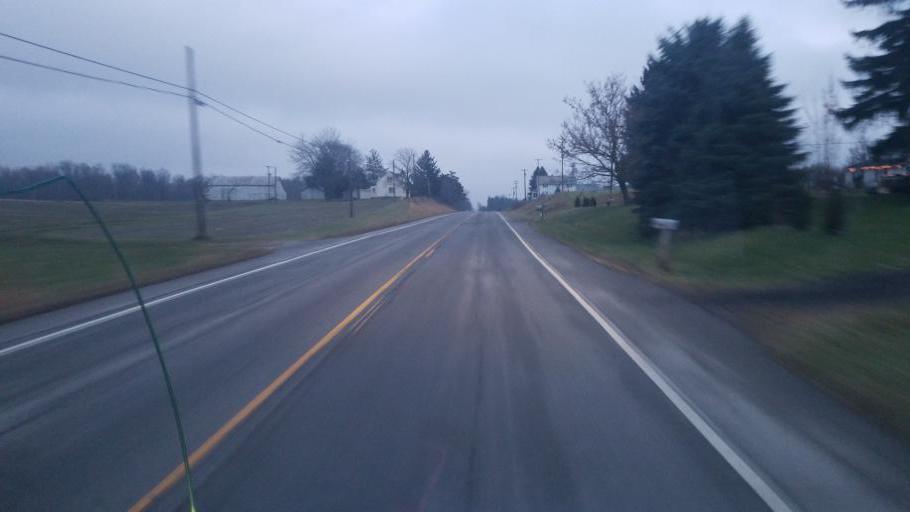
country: US
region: Ohio
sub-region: Crawford County
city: Bucyrus
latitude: 40.8433
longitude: -83.0835
